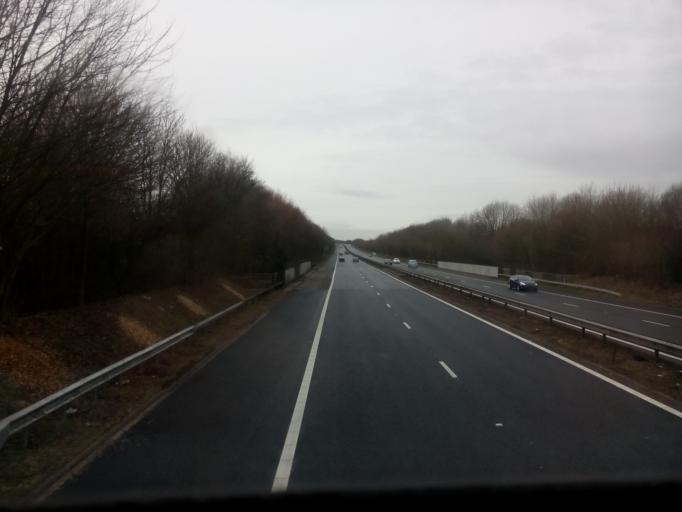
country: GB
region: England
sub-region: Hampshire
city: Kings Worthy
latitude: 51.0908
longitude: -1.2813
